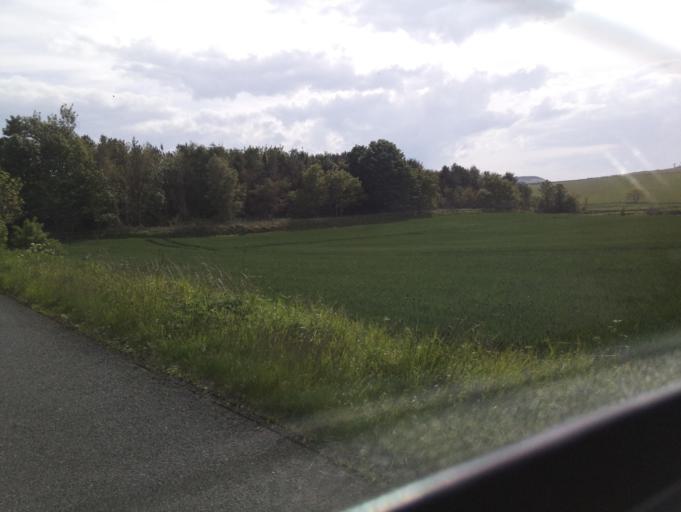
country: GB
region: England
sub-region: Northumberland
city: Ellingham
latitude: 55.4678
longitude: -1.7194
